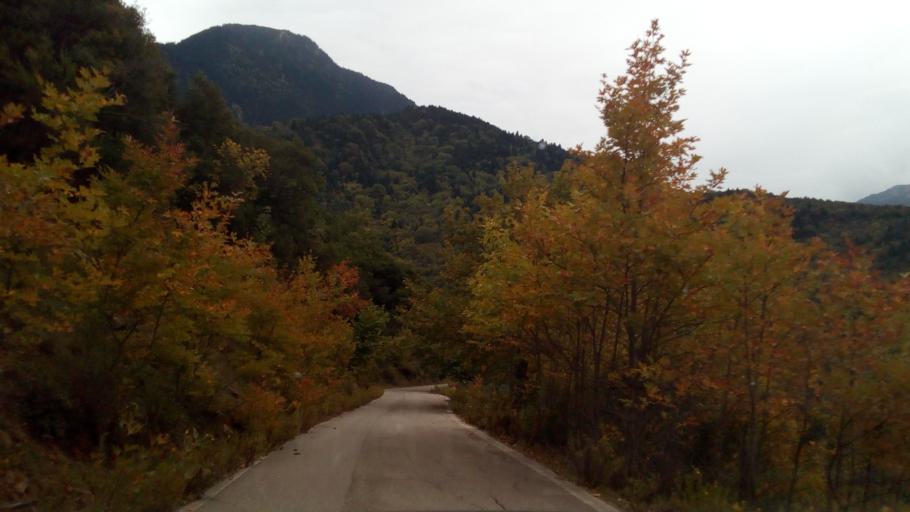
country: GR
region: West Greece
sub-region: Nomos Aitolias kai Akarnanias
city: Thermo
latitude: 38.5976
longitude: 21.8458
